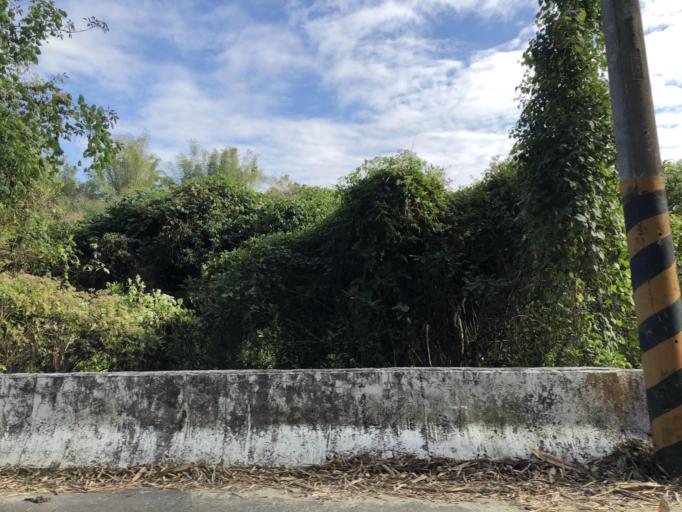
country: TW
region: Taiwan
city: Yujing
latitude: 23.0297
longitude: 120.3928
